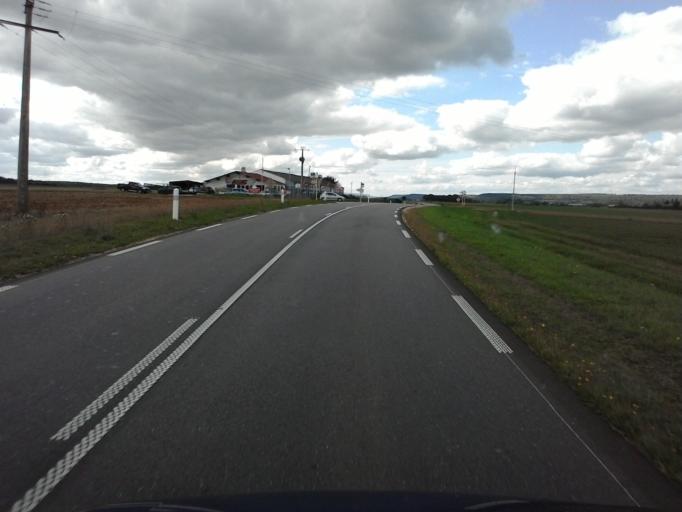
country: FR
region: Lorraine
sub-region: Departement des Vosges
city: Liffol-le-Grand
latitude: 48.3199
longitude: 5.6209
